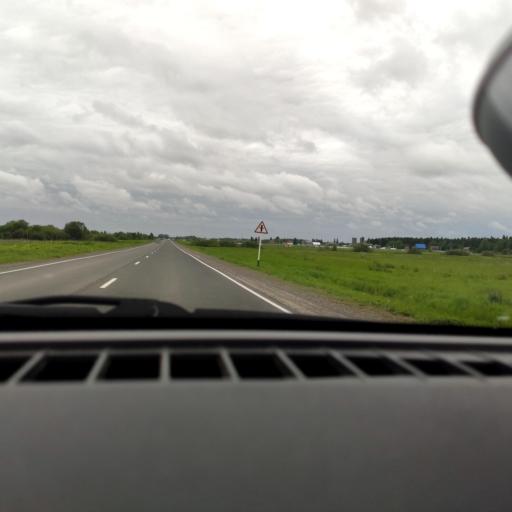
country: RU
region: Perm
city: Ust'-Kachka
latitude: 57.9753
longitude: 55.7216
